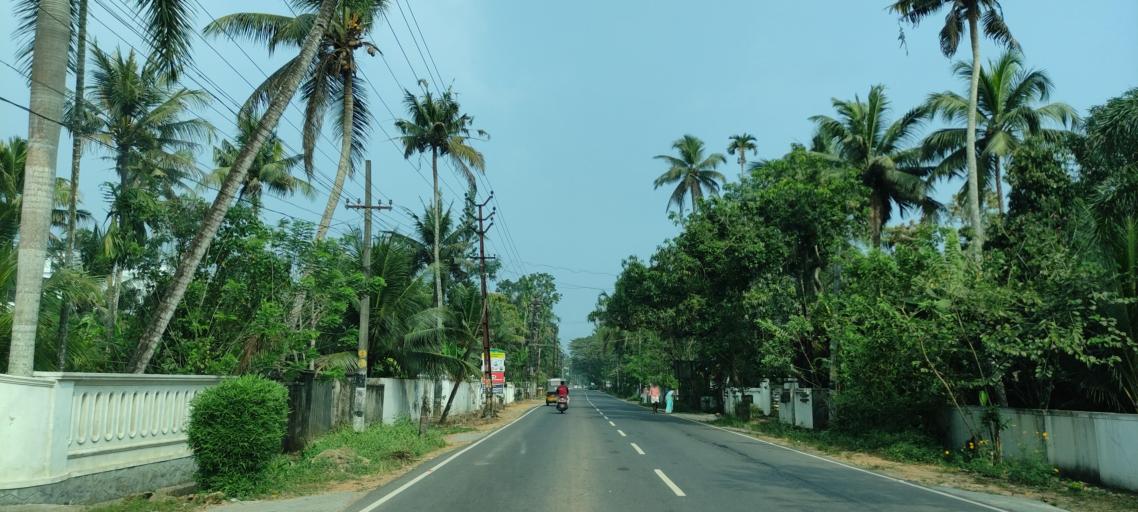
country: IN
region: Kerala
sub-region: Kottayam
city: Vaikam
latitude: 9.7712
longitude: 76.4202
